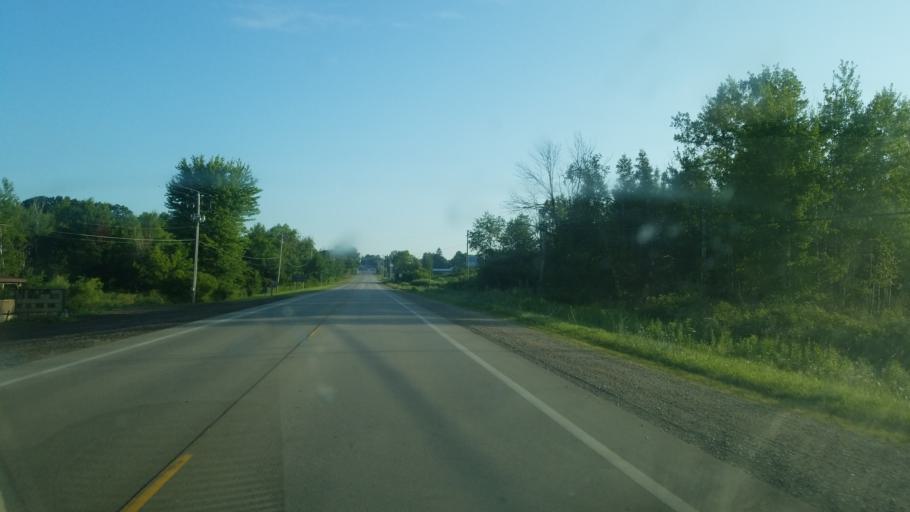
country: US
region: Michigan
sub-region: Montcalm County
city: Stanton
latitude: 43.2850
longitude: -85.0739
